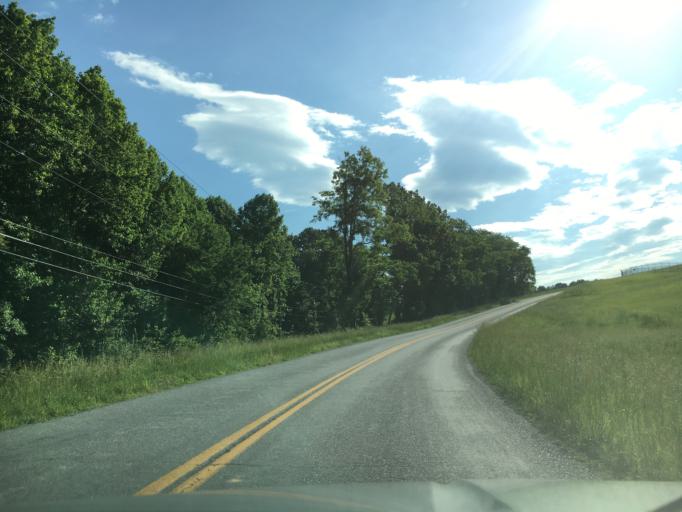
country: US
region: Virginia
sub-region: Campbell County
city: Timberlake
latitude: 37.3359
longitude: -79.2019
